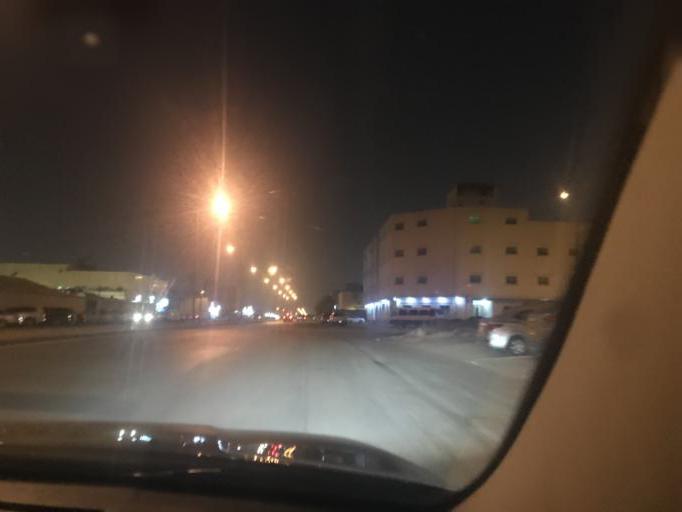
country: SA
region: Ar Riyad
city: Riyadh
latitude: 24.8240
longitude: 46.7401
